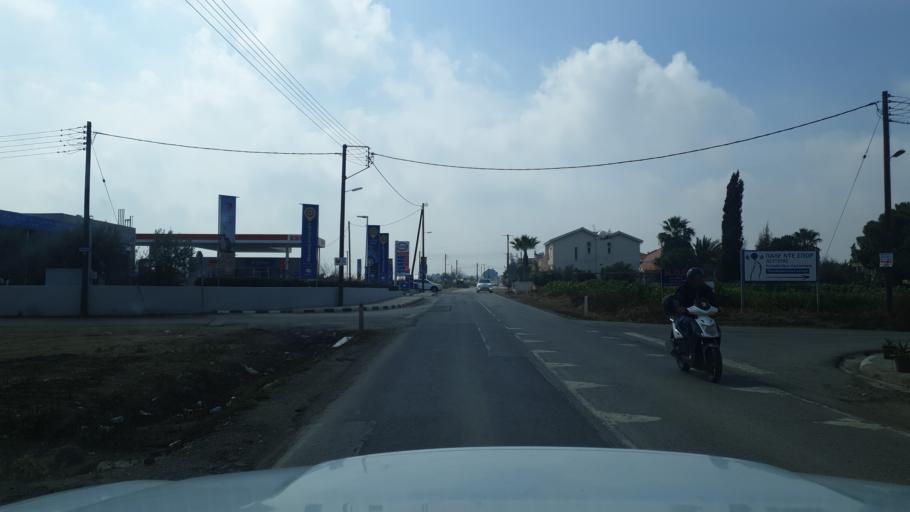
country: CY
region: Lefkosia
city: Kato Deftera
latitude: 35.0815
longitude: 33.2736
